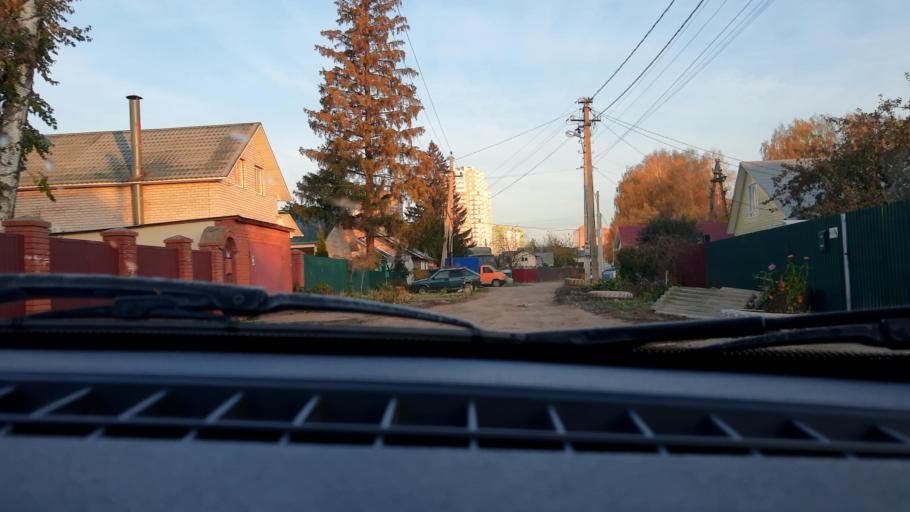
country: RU
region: Bashkortostan
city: Mikhaylovka
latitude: 54.7865
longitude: 55.8767
